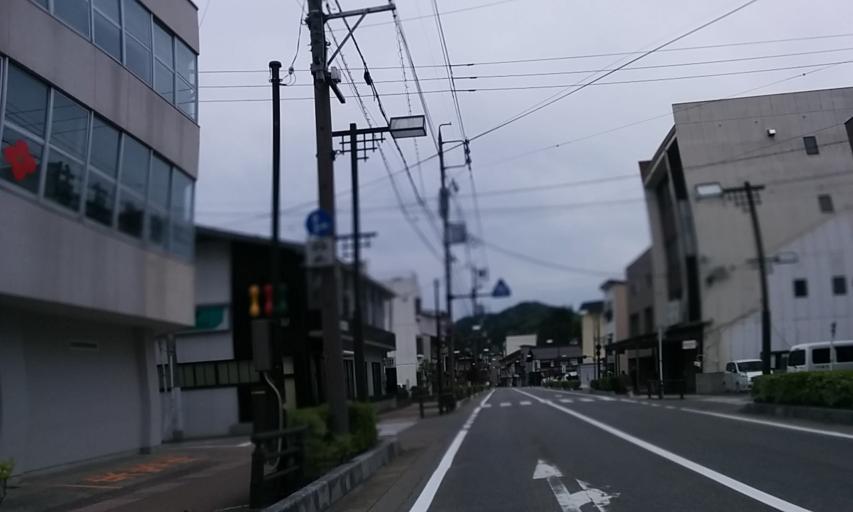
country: JP
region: Gifu
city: Takayama
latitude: 36.1407
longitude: 137.2558
